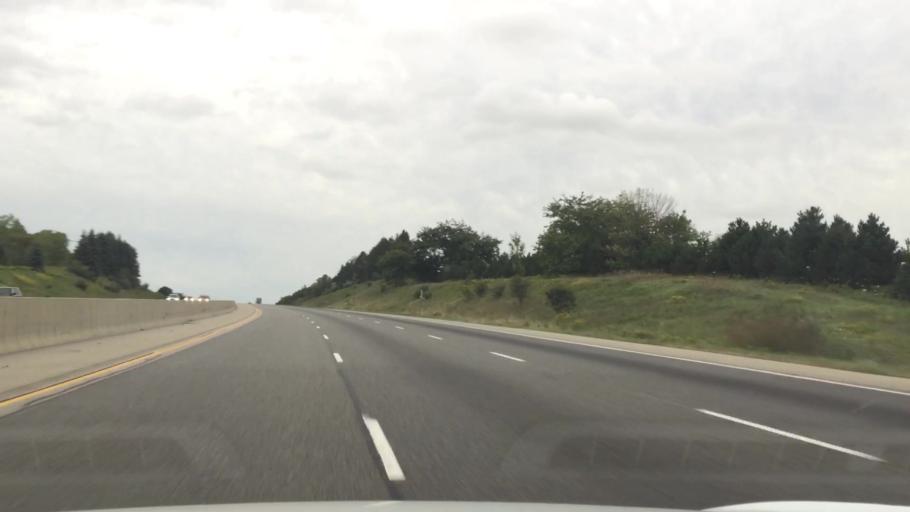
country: CA
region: Ontario
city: Kitchener
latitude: 43.2930
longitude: -80.5003
